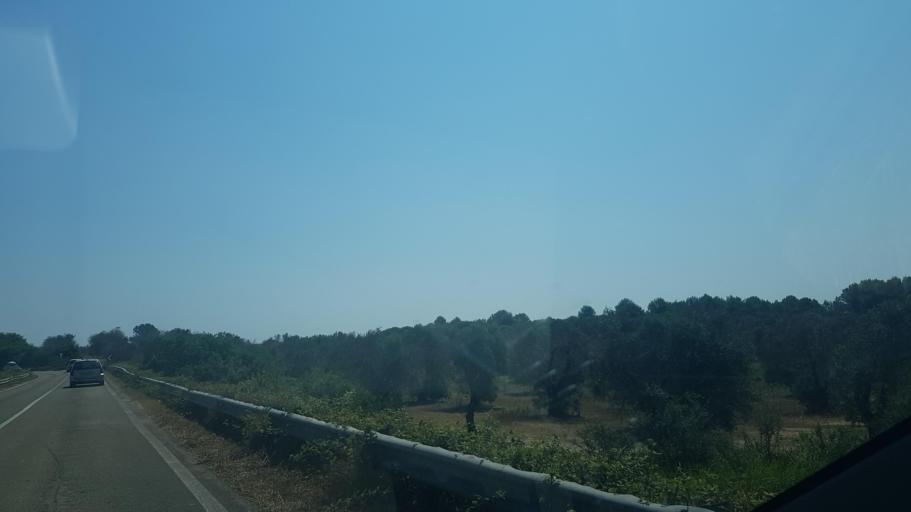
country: IT
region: Apulia
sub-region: Provincia di Lecce
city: Borgagne
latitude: 40.2216
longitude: 18.4259
